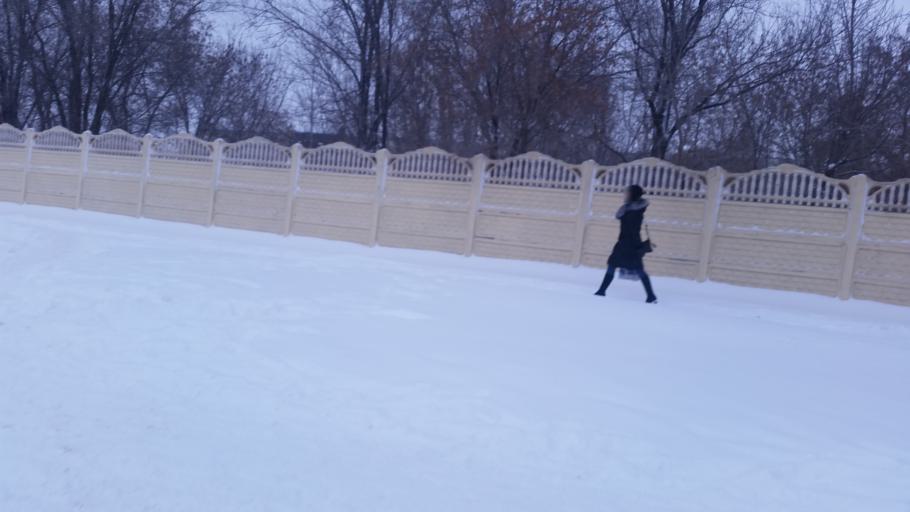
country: KZ
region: Qaraghandy
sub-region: Qaraghandy Qalasy
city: Karagandy
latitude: 49.7685
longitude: 73.1496
